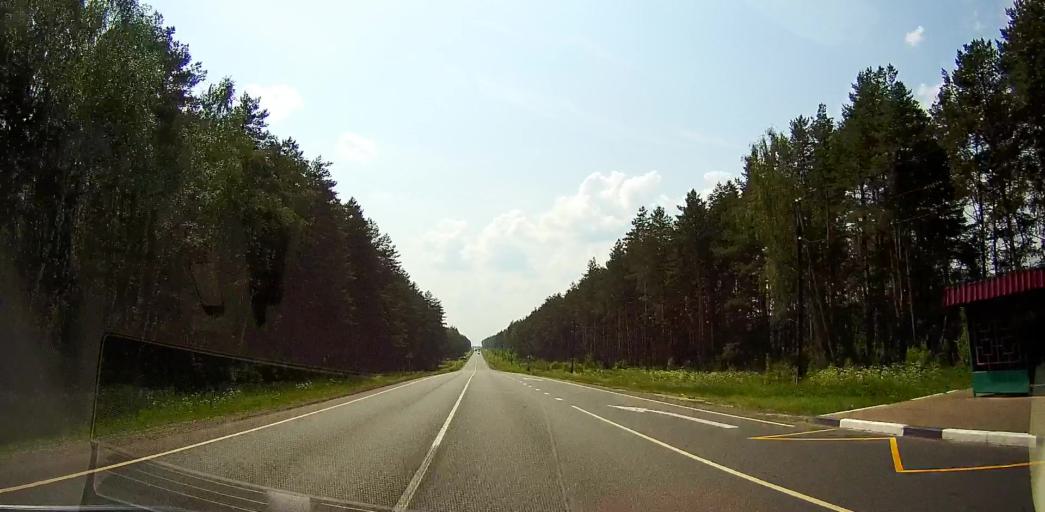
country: RU
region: Moskovskaya
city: Meshcherino
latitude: 55.1720
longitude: 38.3301
